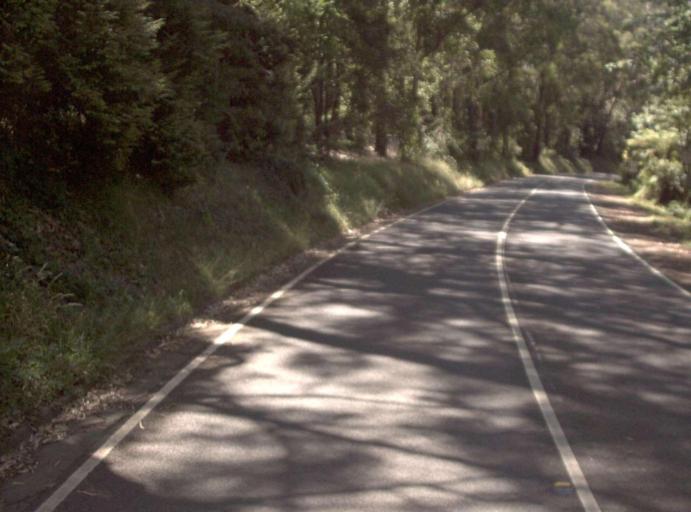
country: AU
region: Victoria
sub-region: Yarra Ranges
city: Kalorama
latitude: -37.8134
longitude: 145.3790
